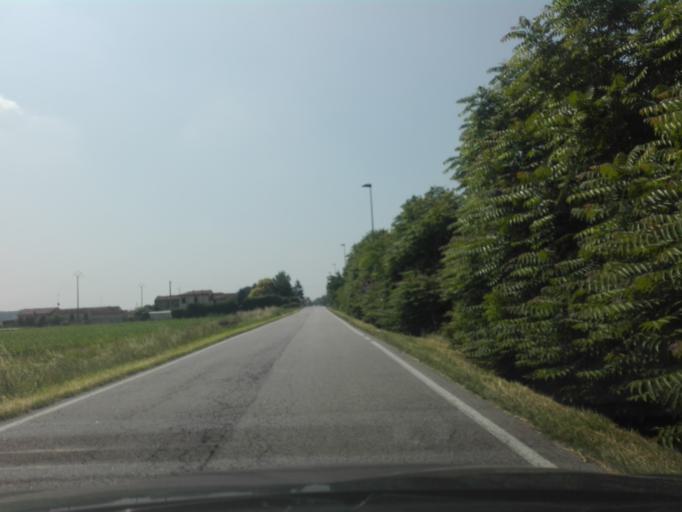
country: IT
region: Veneto
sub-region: Provincia di Rovigo
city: Ceregnano
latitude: 45.0607
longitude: 11.8693
